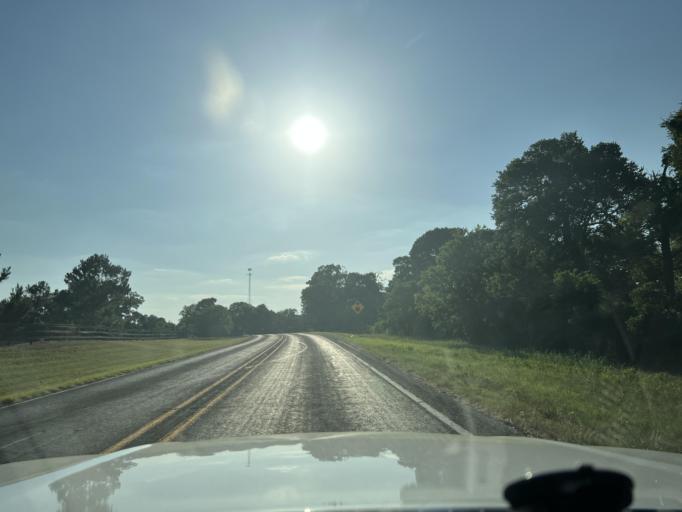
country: US
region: Texas
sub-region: Washington County
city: Brenham
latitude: 30.2338
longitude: -96.2812
